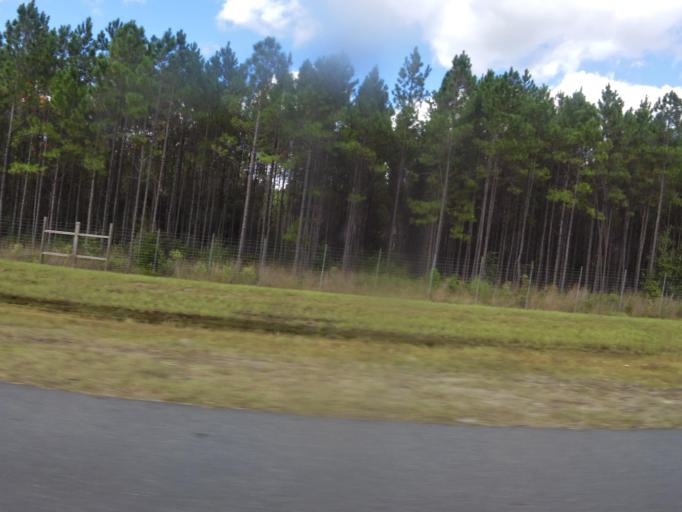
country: US
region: Florida
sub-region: Bradford County
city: Starke
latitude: 29.9864
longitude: -82.1090
